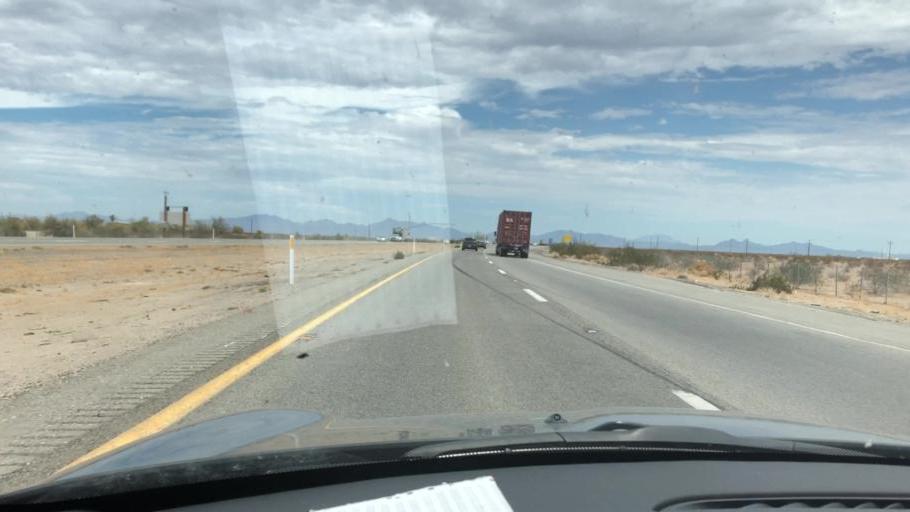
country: US
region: California
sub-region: Riverside County
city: Mesa Verde
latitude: 33.6088
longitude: -114.7221
